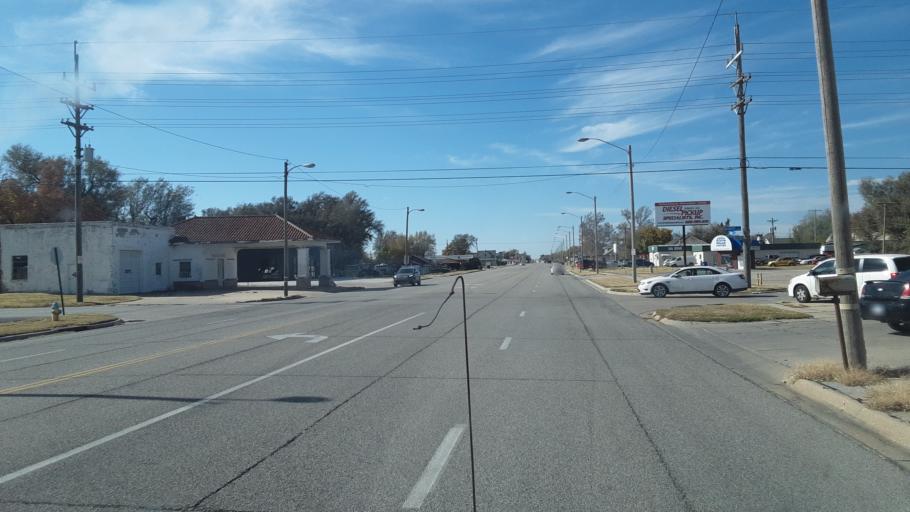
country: US
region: Kansas
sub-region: McPherson County
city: McPherson
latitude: 38.3693
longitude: -97.6759
